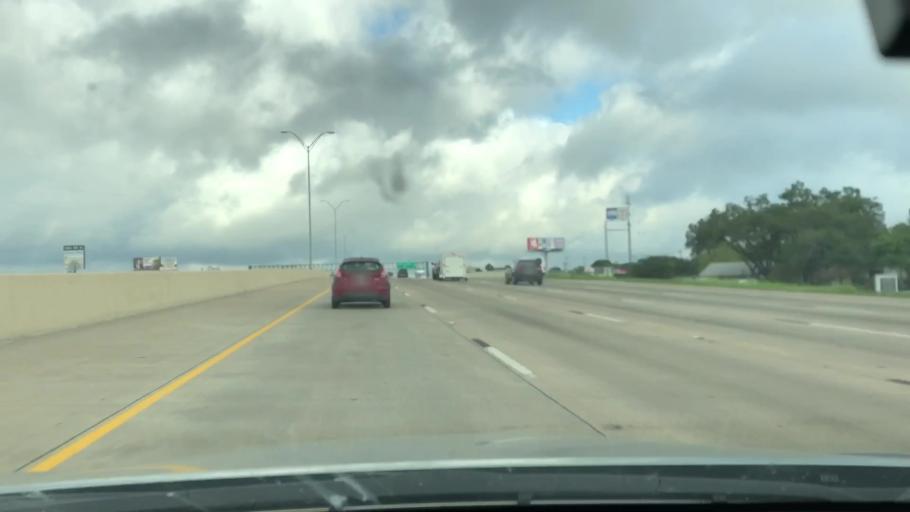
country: US
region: Texas
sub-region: Bexar County
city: Balcones Heights
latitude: 29.4805
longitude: -98.5245
